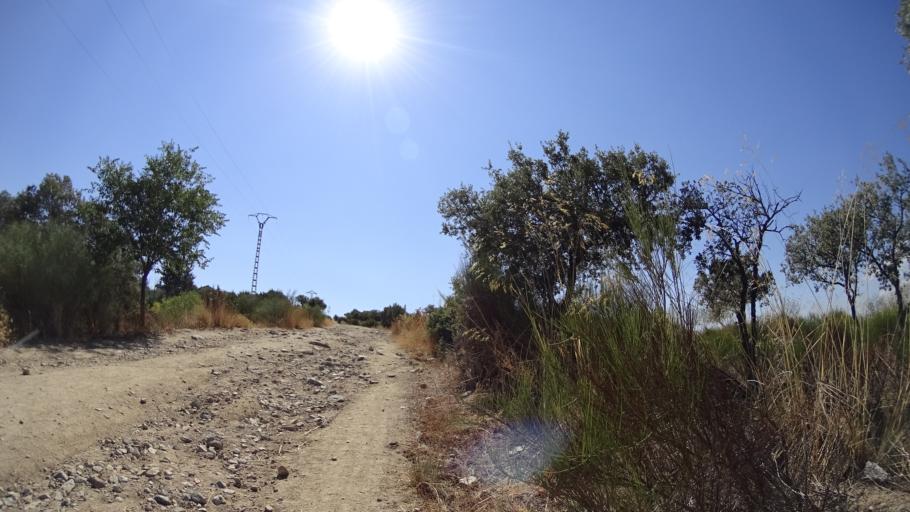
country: ES
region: Madrid
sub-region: Provincia de Madrid
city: Collado-Villalba
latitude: 40.6073
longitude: -4.0115
